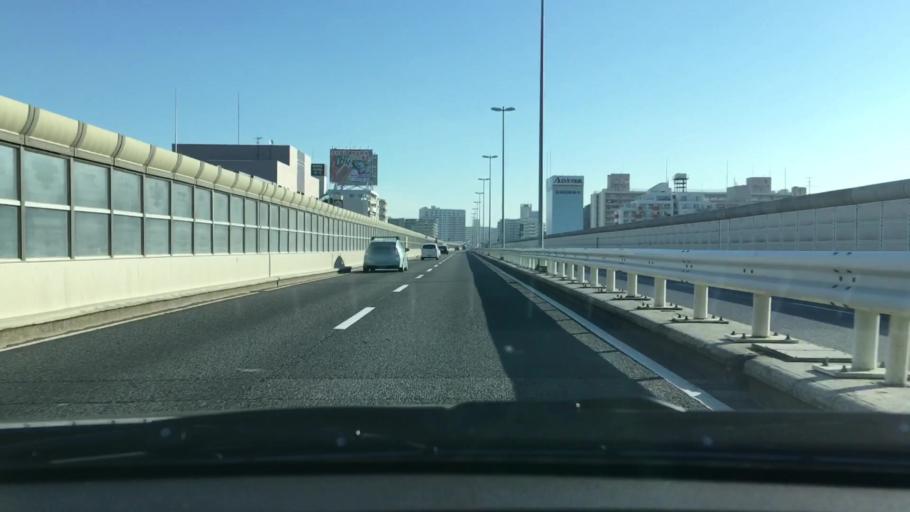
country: JP
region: Tokyo
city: Urayasu
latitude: 35.6941
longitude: 139.8355
